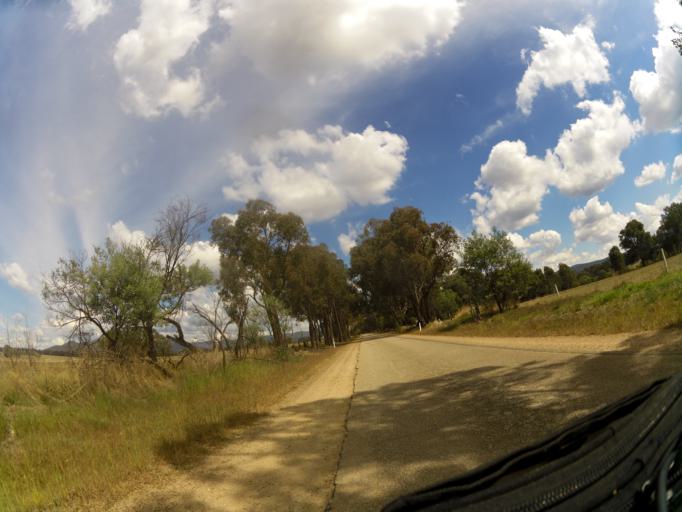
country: AU
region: Victoria
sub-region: Benalla
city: Benalla
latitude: -36.7511
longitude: 145.9826
